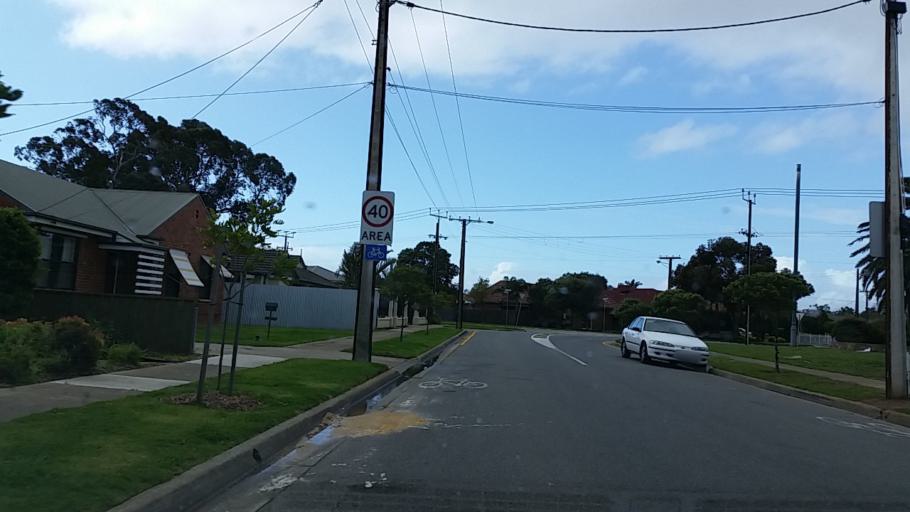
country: AU
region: South Australia
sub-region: Charles Sturt
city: Woodville West
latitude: -34.8852
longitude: 138.5255
